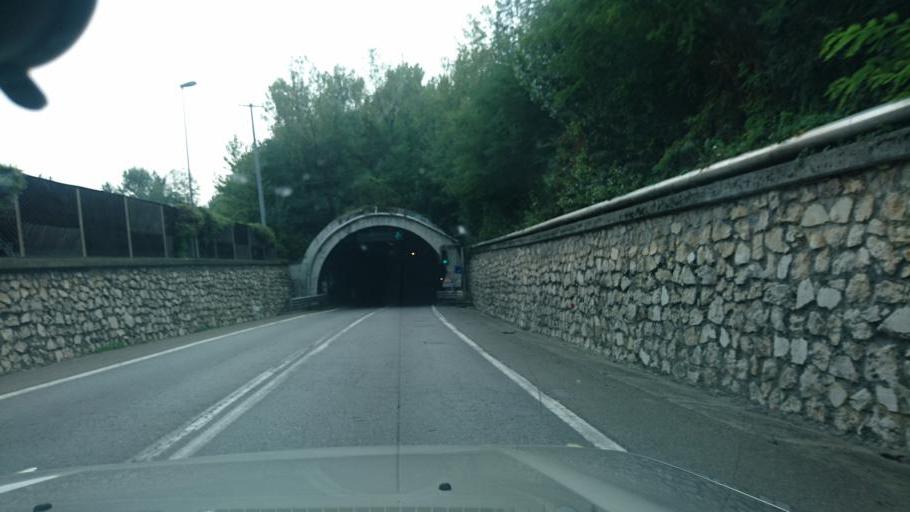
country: IT
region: Lombardy
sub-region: Provincia di Brescia
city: Roe Volciano
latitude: 45.6178
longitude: 10.4807
